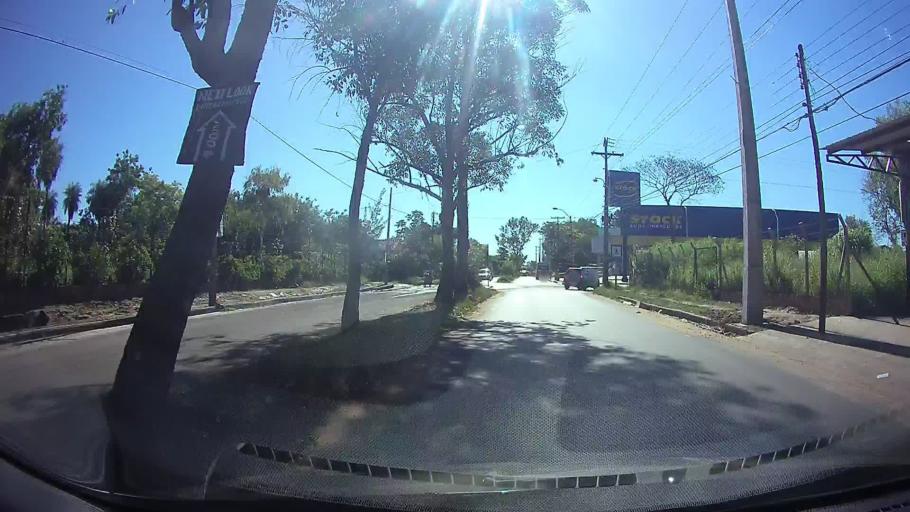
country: PY
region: Central
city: Fernando de la Mora
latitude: -25.2964
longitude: -57.5220
